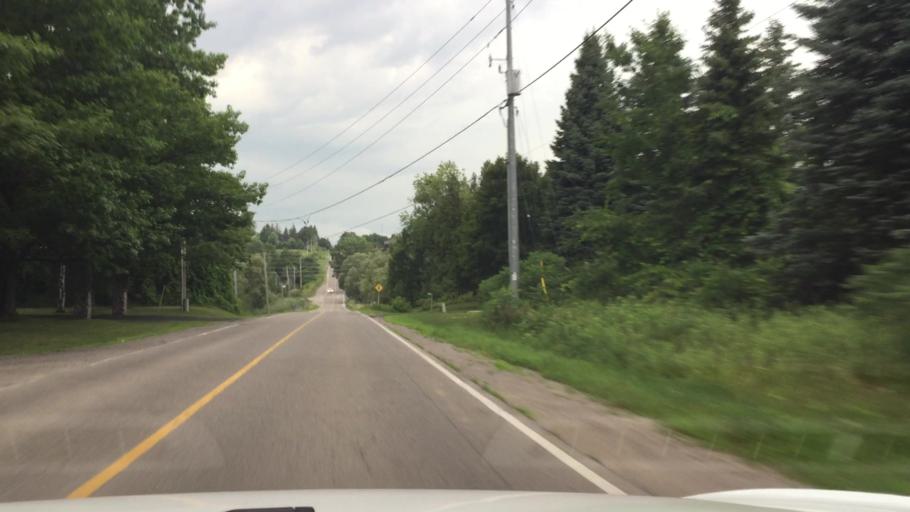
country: CA
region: Ontario
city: Oshawa
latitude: 43.9334
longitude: -78.7982
